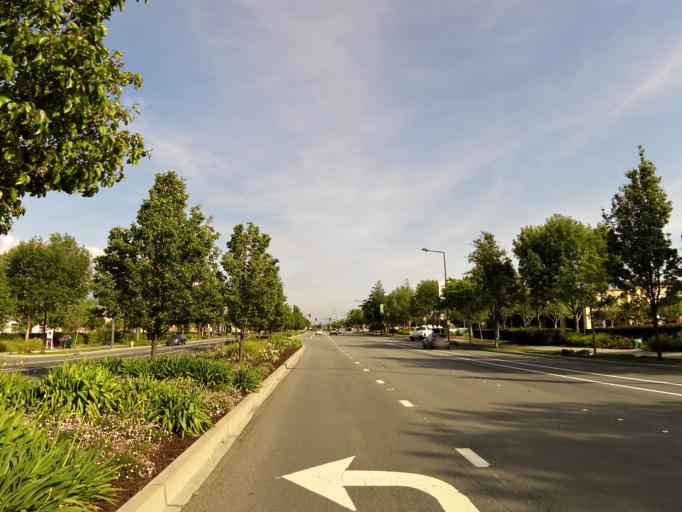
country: US
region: California
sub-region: Alameda County
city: Fremont
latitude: 37.5051
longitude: -121.9707
